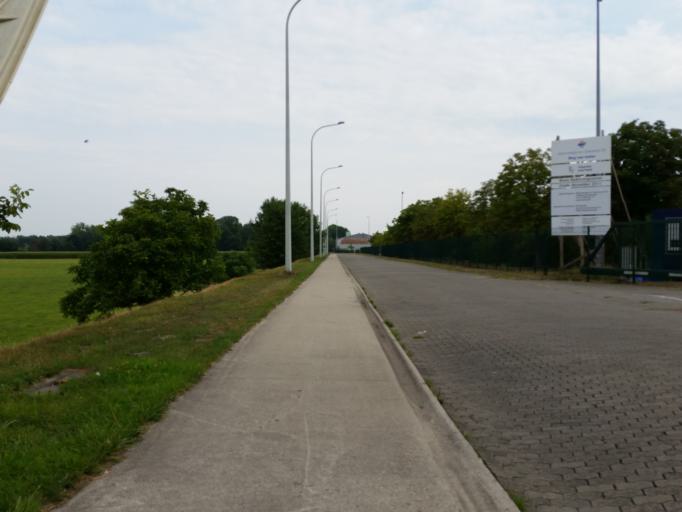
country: BE
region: Flanders
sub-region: Provincie Vlaams-Brabant
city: Kapelle-op-den-Bos
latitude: 51.0004
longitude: 4.3732
